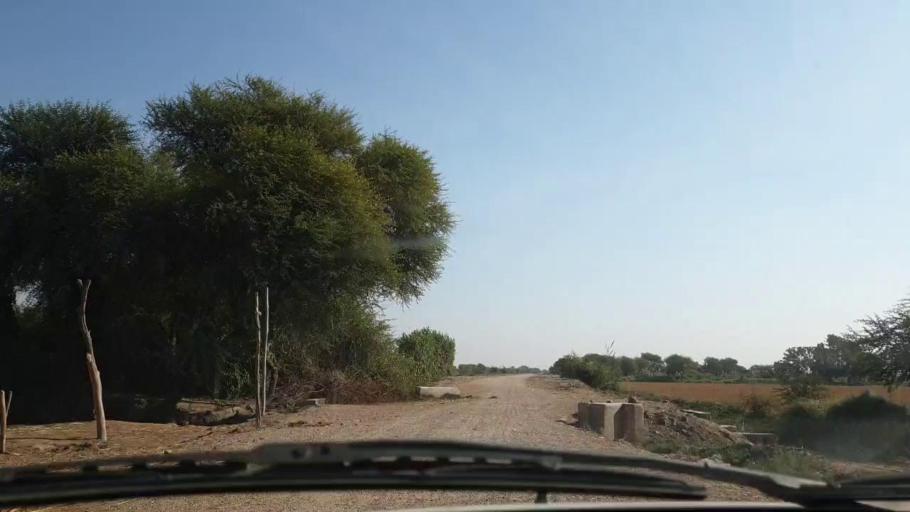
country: PK
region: Sindh
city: Bulri
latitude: 24.8023
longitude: 68.3924
